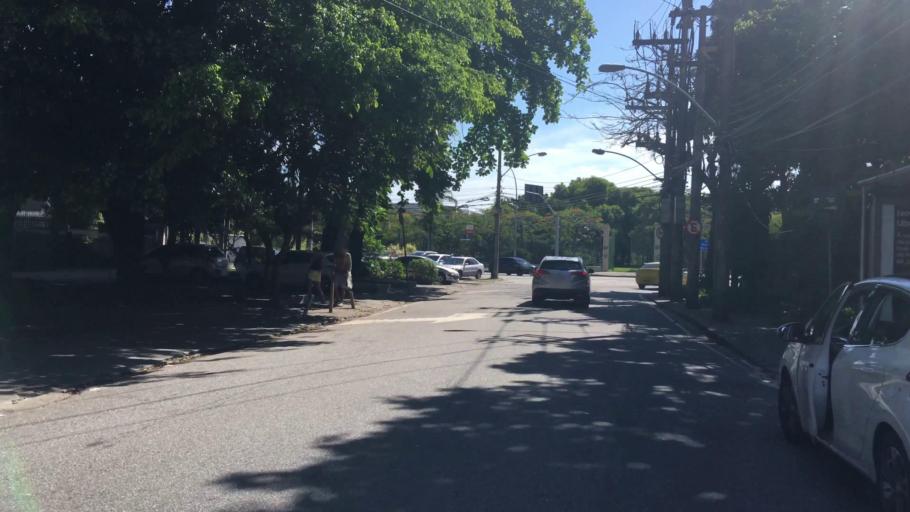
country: BR
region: Rio de Janeiro
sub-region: Rio De Janeiro
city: Rio de Janeiro
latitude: -23.0103
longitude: -43.3082
